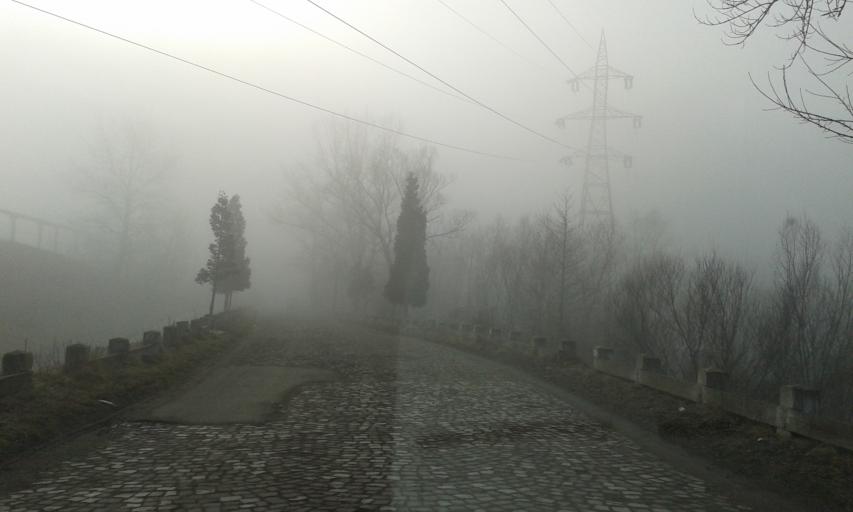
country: RO
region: Hunedoara
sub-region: Municipiul  Vulcan
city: Jiu-Paroseni
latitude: 45.3671
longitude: 23.2666
